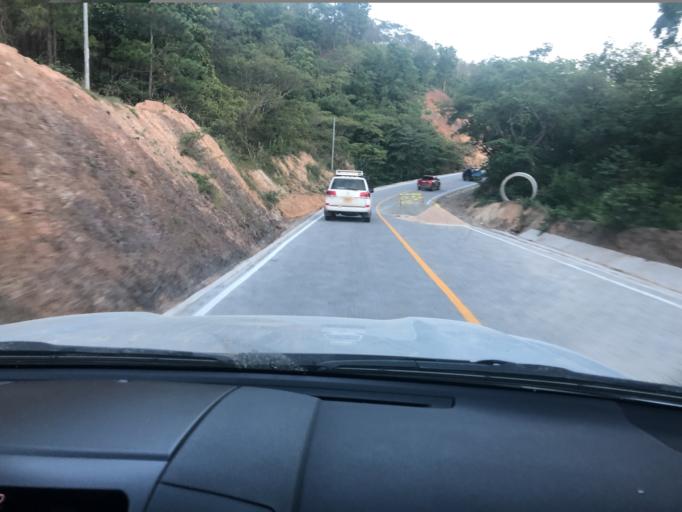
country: NI
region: Nueva Segovia
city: Ocotal
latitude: 13.6724
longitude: -86.6149
